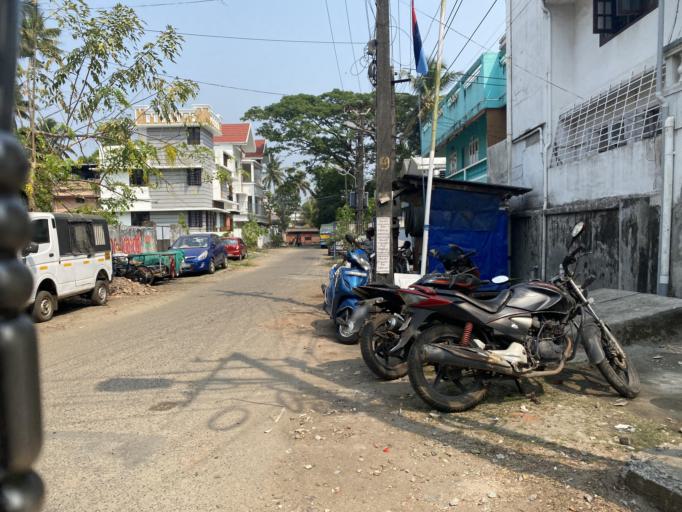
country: IN
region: Kerala
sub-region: Ernakulam
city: Cochin
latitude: 9.9542
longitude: 76.2445
